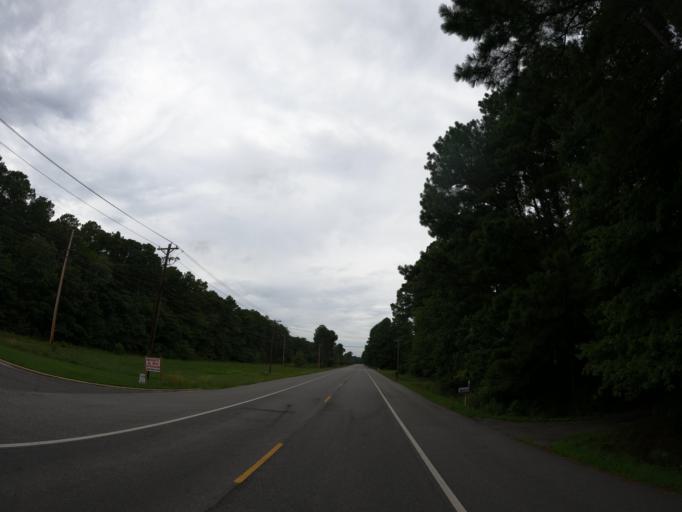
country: US
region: Maryland
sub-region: Saint Mary's County
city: Lexington Park
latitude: 38.1590
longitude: -76.5240
